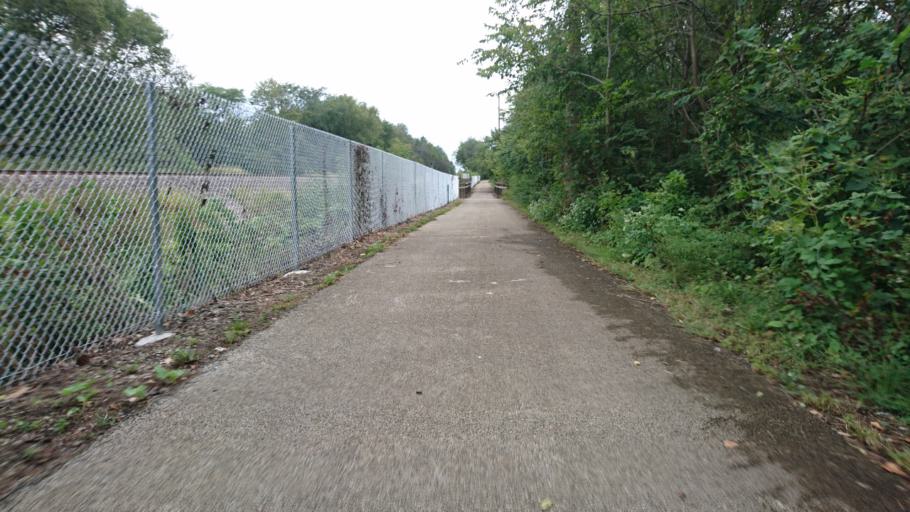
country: US
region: Illinois
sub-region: Sangamon County
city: Southern View
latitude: 39.7249
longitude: -89.6770
